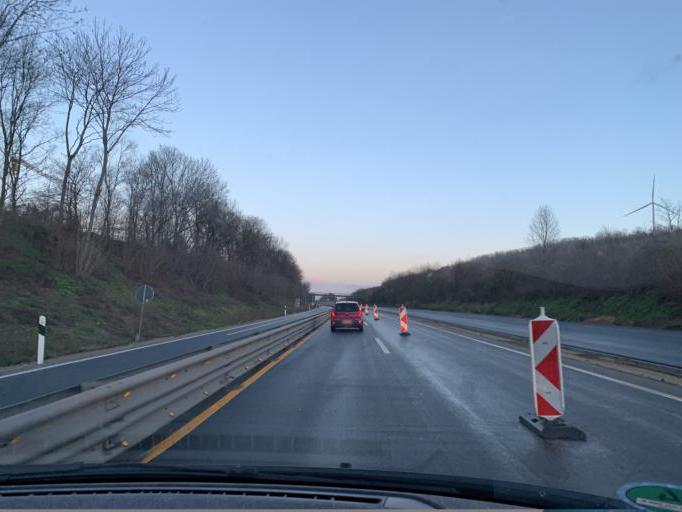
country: DE
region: North Rhine-Westphalia
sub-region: Regierungsbezirk Dusseldorf
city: Grevenbroich
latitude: 51.0754
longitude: 6.5975
